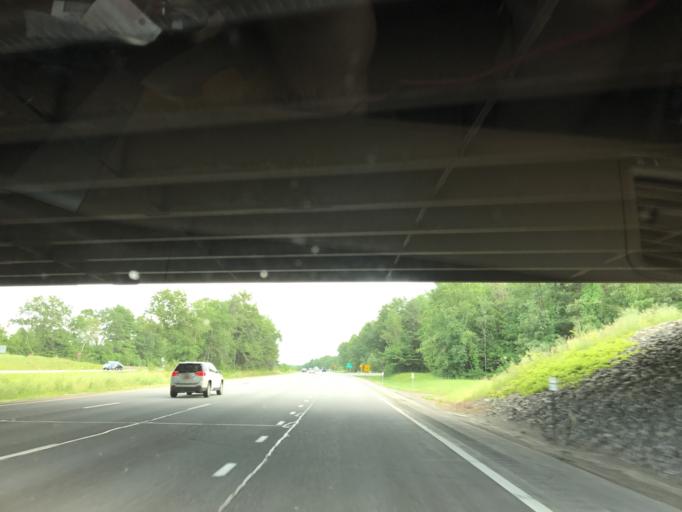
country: US
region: New York
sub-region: Warren County
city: Glens Falls North
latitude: 43.3301
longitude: -73.6844
